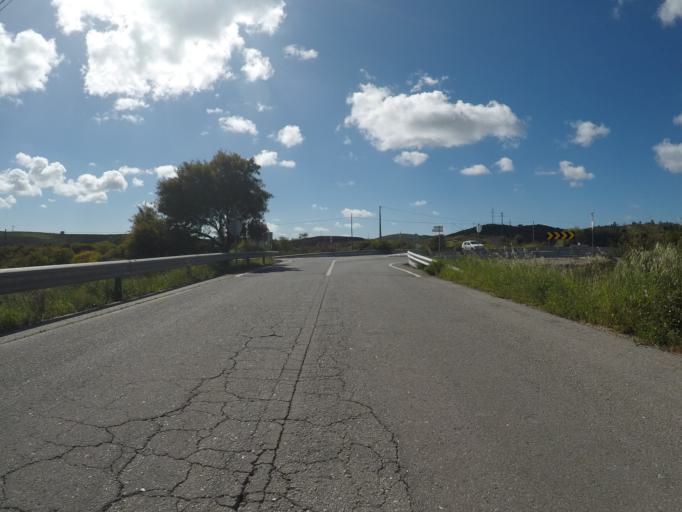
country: PT
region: Faro
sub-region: Vila do Bispo
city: Vila do Bispo
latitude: 37.0784
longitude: -8.8352
